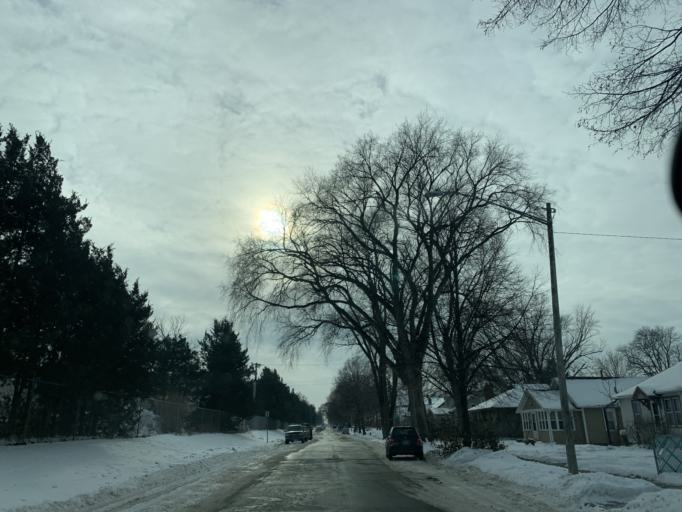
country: US
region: Minnesota
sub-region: Dakota County
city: Mendota Heights
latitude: 44.9043
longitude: -93.2076
